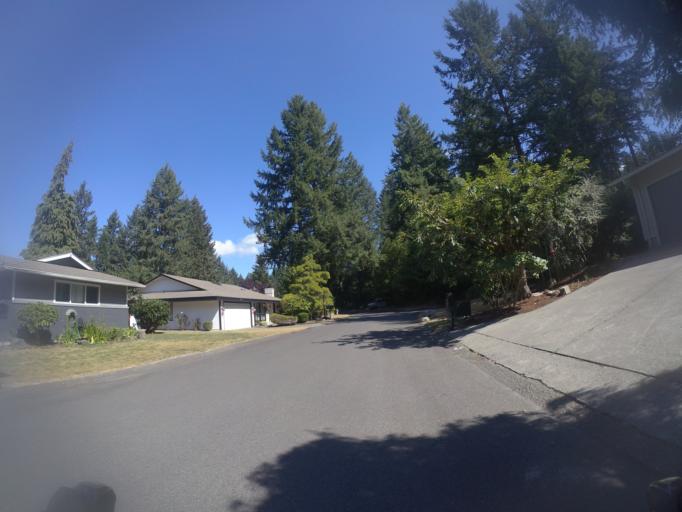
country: US
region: Washington
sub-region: Pierce County
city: University Place
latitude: 47.2160
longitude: -122.5573
